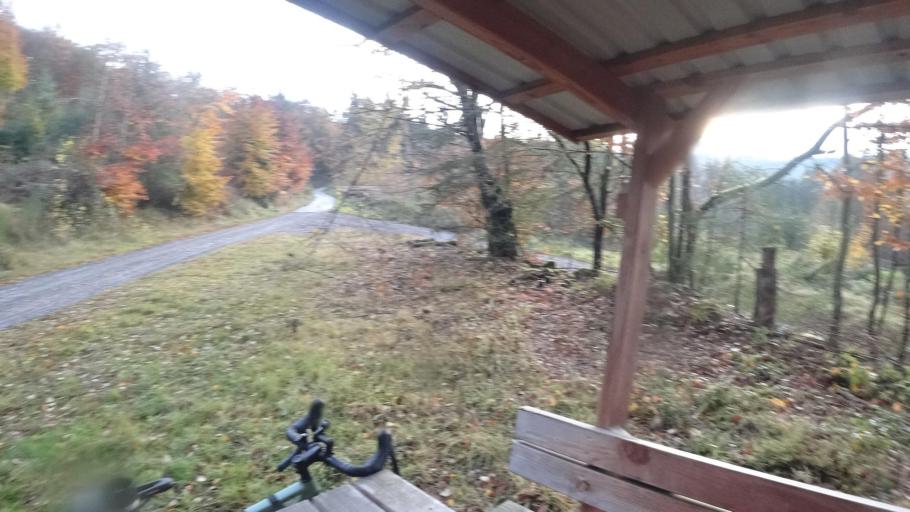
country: DE
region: Rheinland-Pfalz
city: Gondershausen
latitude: 50.1373
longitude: 7.5025
